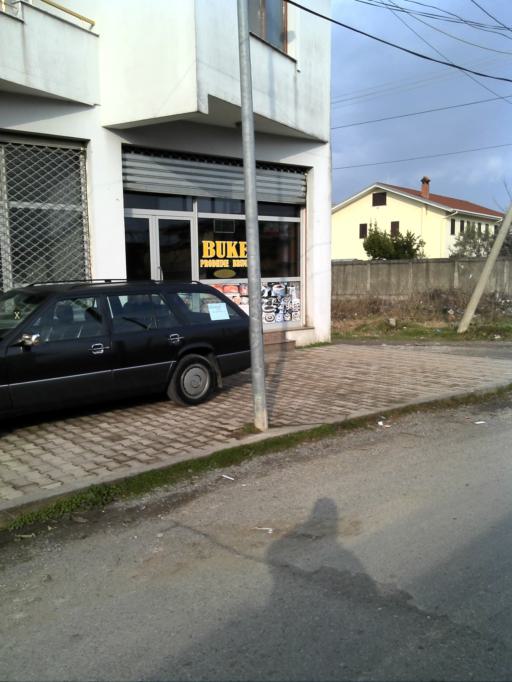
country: AL
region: Shkoder
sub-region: Rrethi i Shkodres
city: Shkoder
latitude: 42.0569
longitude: 19.5156
